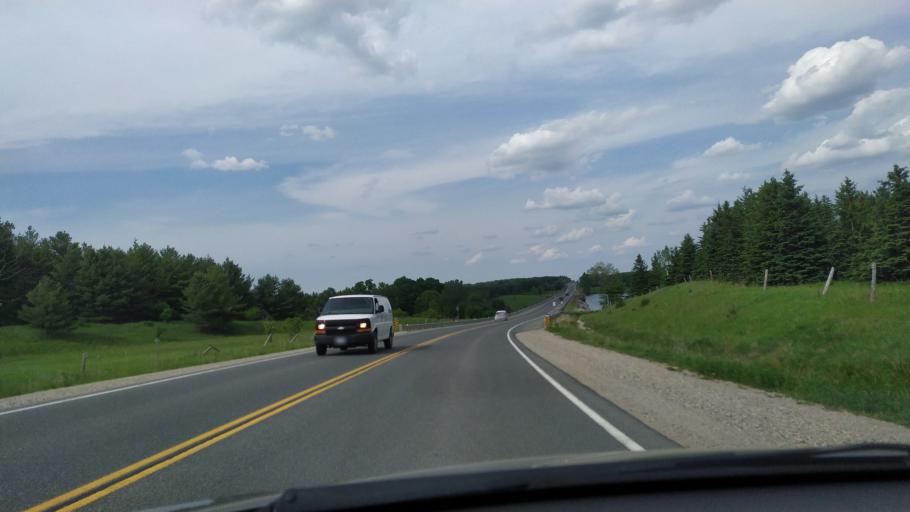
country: CA
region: Ontario
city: Stratford
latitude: 43.2585
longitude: -81.0775
